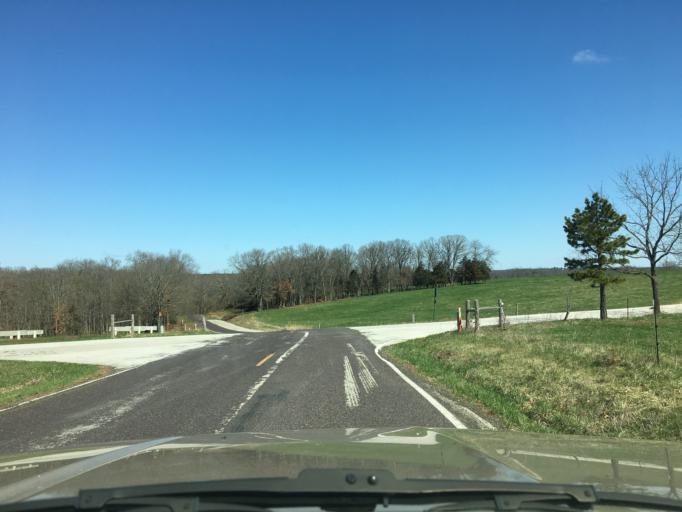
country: US
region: Missouri
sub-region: Franklin County
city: New Haven
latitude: 38.5394
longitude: -91.3290
